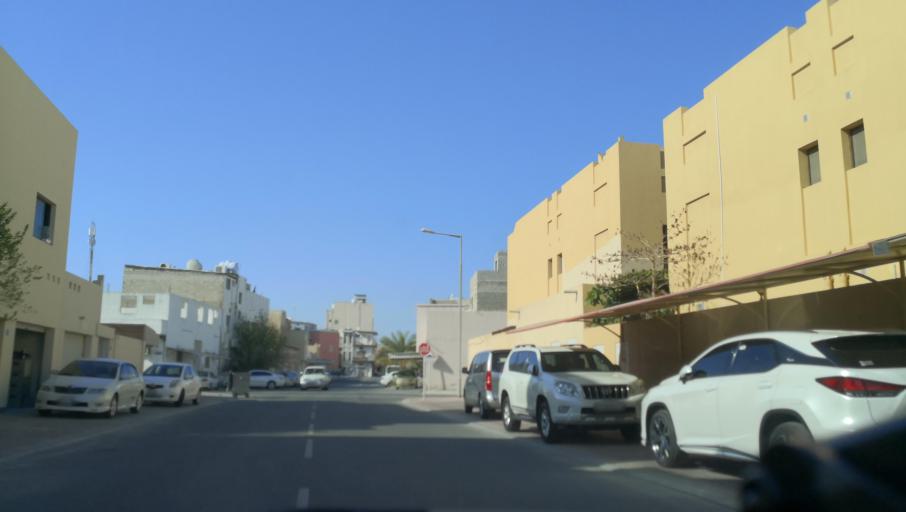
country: BH
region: Muharraq
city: Al Hadd
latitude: 26.2504
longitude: 50.6333
